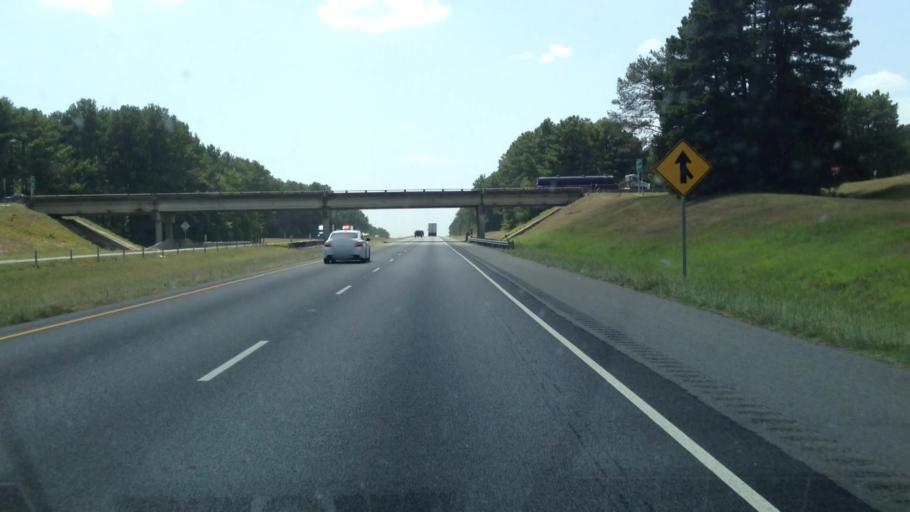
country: US
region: Louisiana
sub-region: Webster Parish
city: Minden
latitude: 32.5629
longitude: -93.1577
